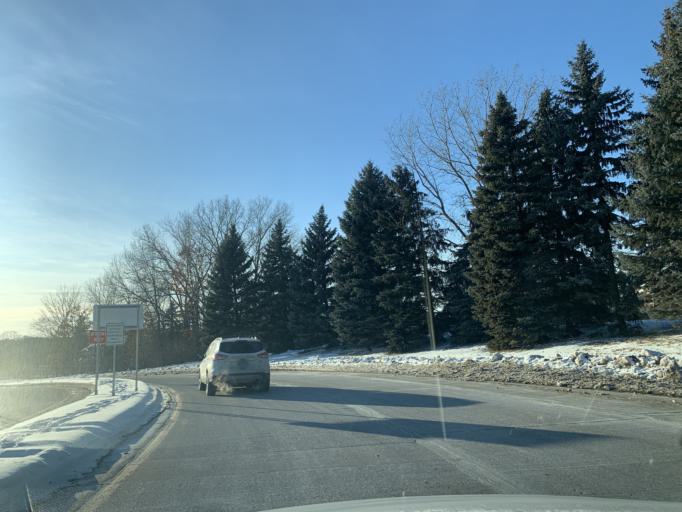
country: US
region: Minnesota
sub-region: Hennepin County
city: Wayzata
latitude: 44.9724
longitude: -93.4704
